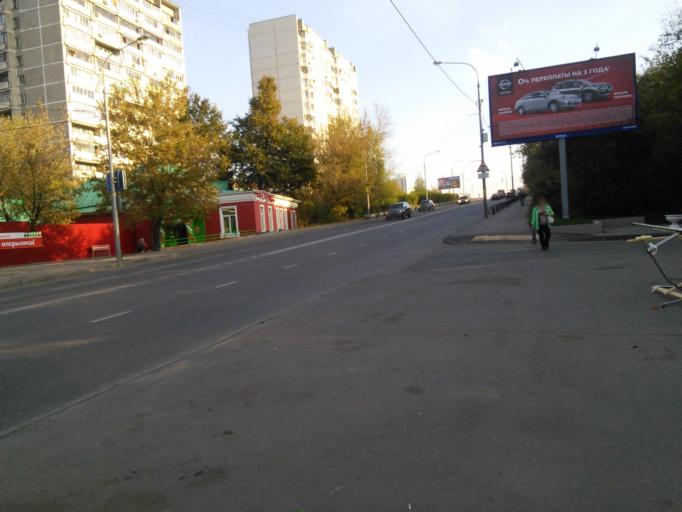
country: RU
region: Moscow
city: Zapadnoye Degunino
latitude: 55.8439
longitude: 37.5217
